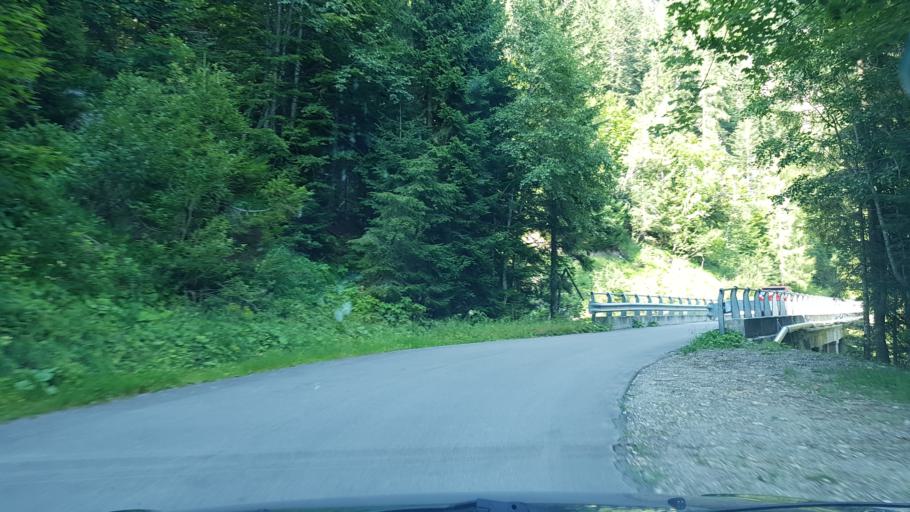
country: IT
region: Friuli Venezia Giulia
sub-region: Provincia di Udine
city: Sauris di Sotto
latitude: 46.4761
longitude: 12.6560
